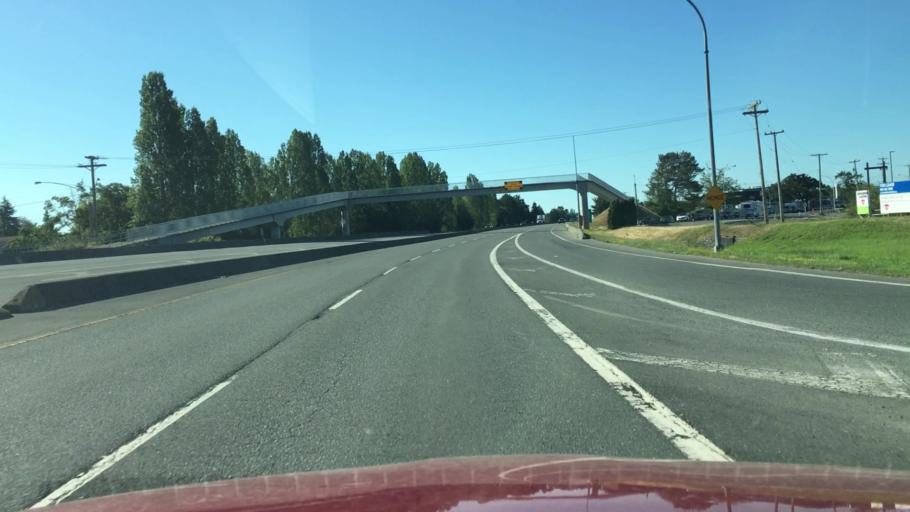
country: CA
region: British Columbia
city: North Saanich
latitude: 48.6630
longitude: -123.4175
